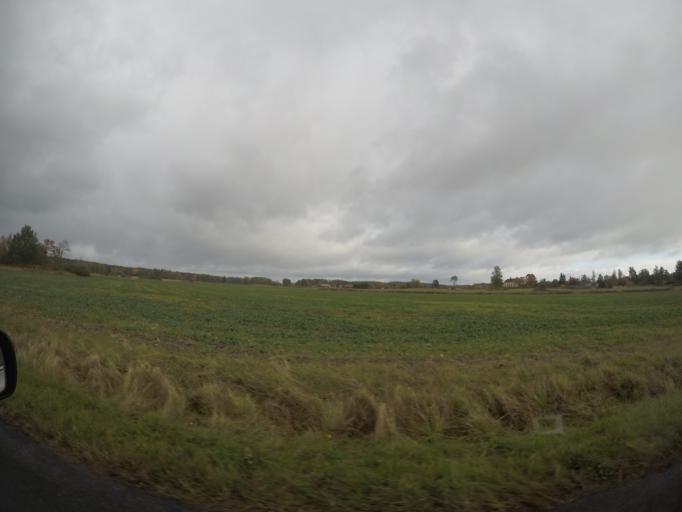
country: SE
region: Soedermanland
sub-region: Eskilstuna Kommun
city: Kvicksund
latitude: 59.3229
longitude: 16.3038
